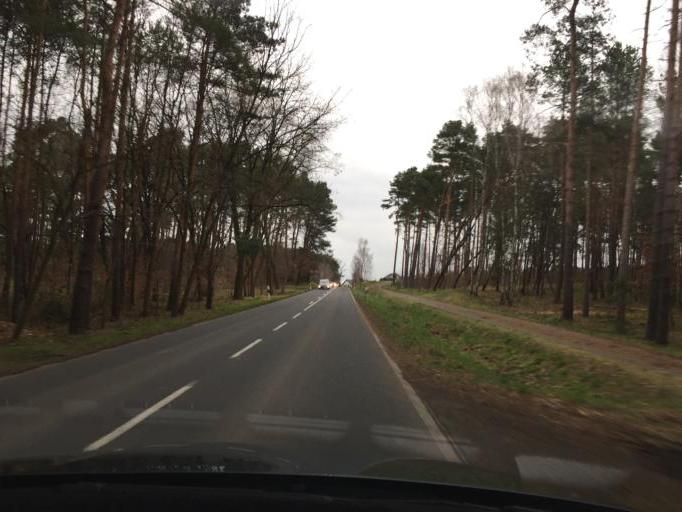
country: DE
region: Brandenburg
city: Gross Lindow
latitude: 52.1046
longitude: 14.5012
